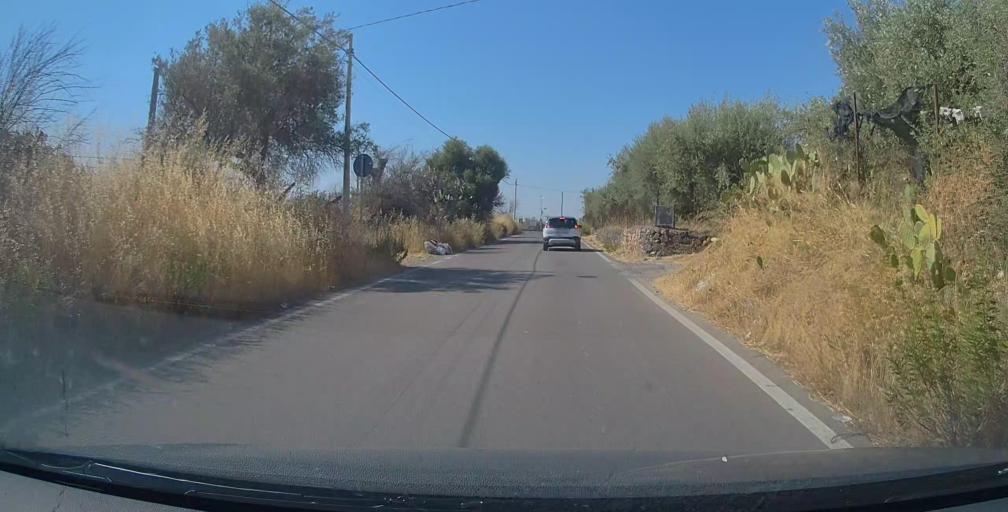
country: IT
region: Sicily
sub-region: Catania
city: Palazzolo
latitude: 37.5424
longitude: 14.9300
